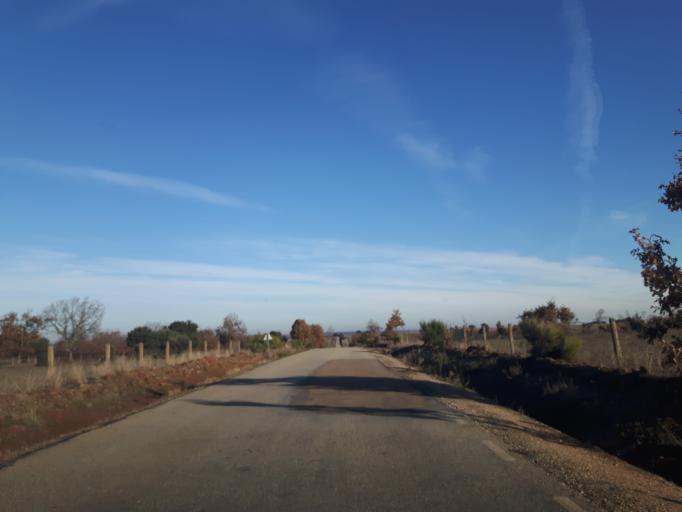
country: ES
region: Castille and Leon
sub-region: Provincia de Salamanca
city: Olmedo de Camaces
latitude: 40.9103
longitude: -6.6186
